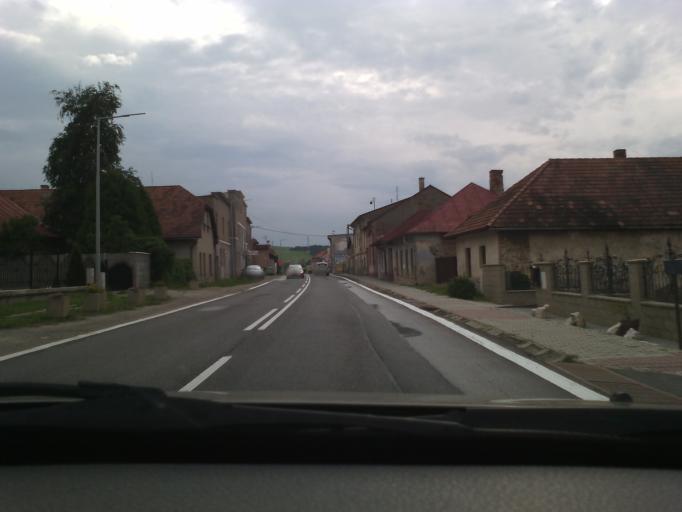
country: SK
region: Presovsky
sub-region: Okres Presov
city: Kezmarok
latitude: 49.1181
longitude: 20.3814
